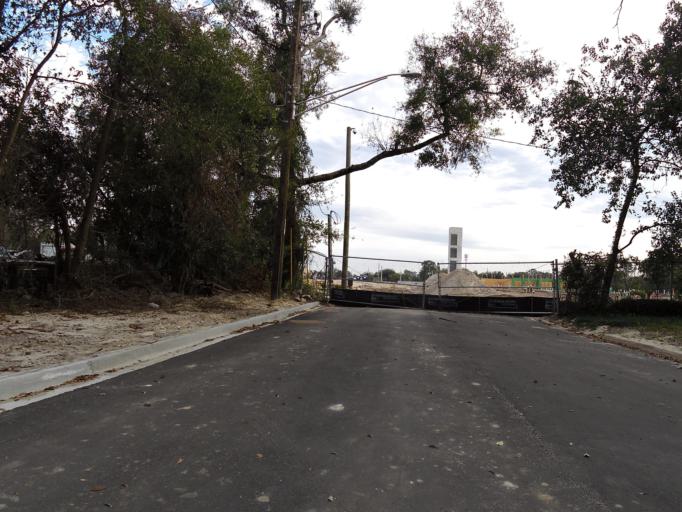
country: US
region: Florida
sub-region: Nassau County
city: Hilliard
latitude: 30.5851
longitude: -82.1600
